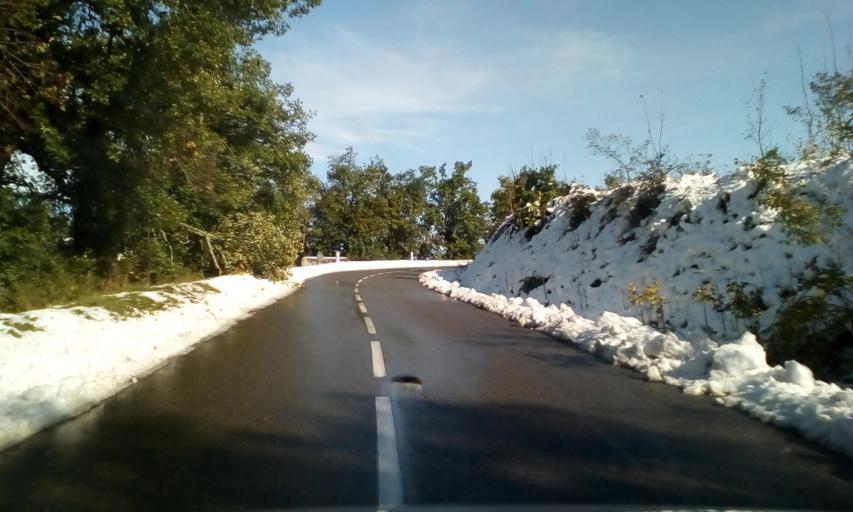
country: FR
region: Rhone-Alpes
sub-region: Departement de l'Ardeche
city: Quintenas
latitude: 45.1568
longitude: 4.6988
